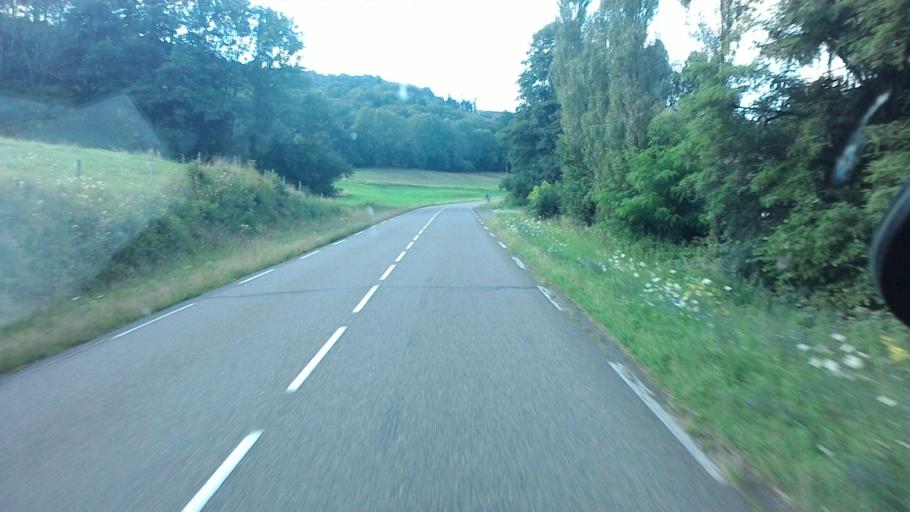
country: FR
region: Franche-Comte
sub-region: Departement de la Haute-Saone
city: Melisey
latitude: 47.8591
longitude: 6.5672
